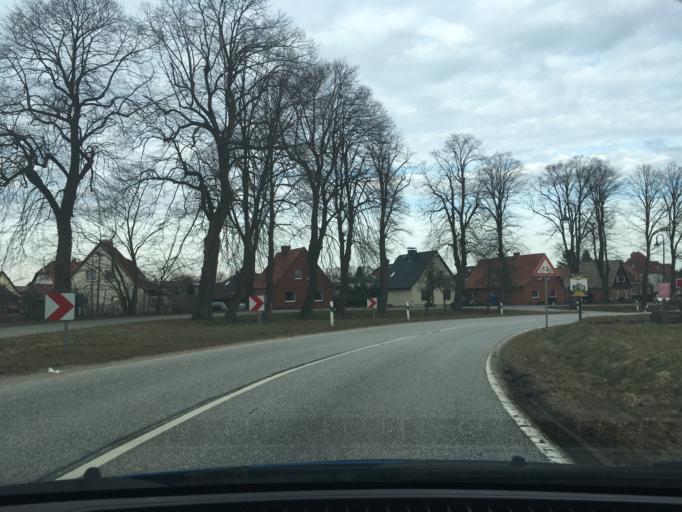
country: DE
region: Mecklenburg-Vorpommern
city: Zarrentin
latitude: 53.5470
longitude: 10.9092
